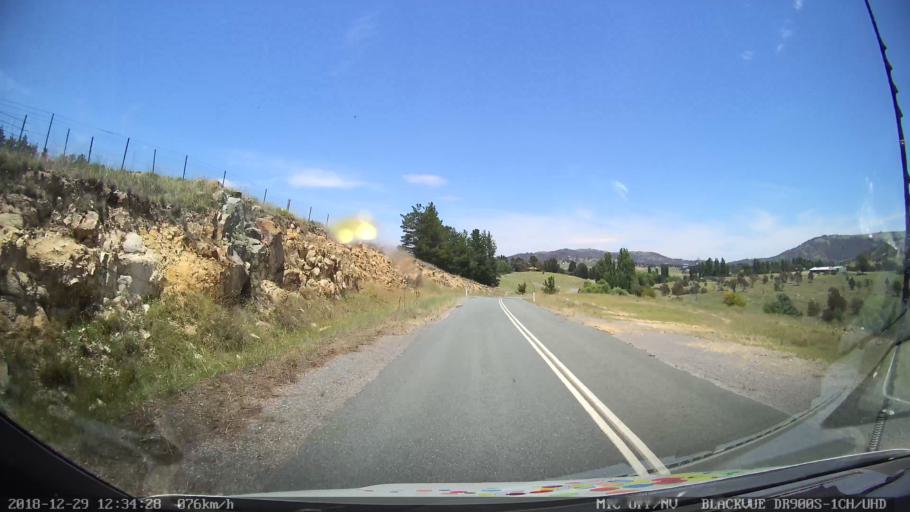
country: AU
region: Australian Capital Territory
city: Macarthur
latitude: -35.5525
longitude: 149.2263
